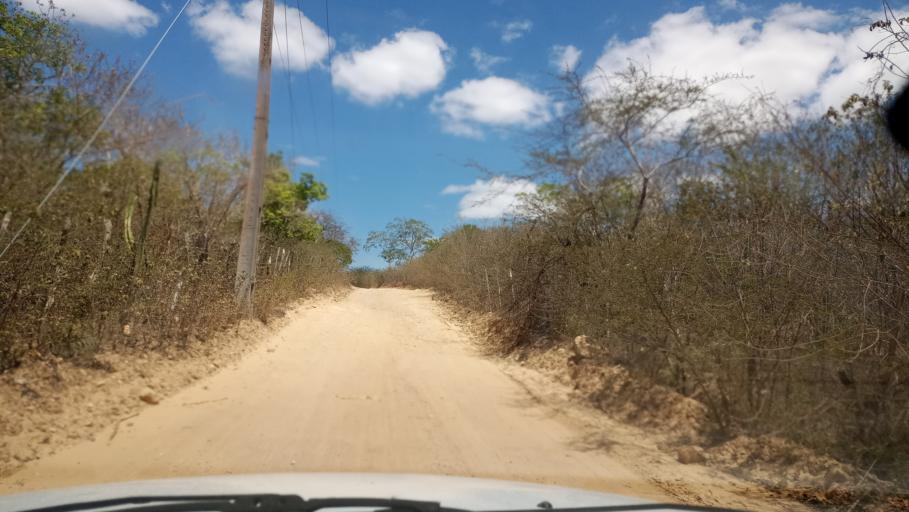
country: BR
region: Rio Grande do Norte
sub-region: Sao Paulo Do Potengi
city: Sao Paulo do Potengi
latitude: -5.7929
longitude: -35.9203
